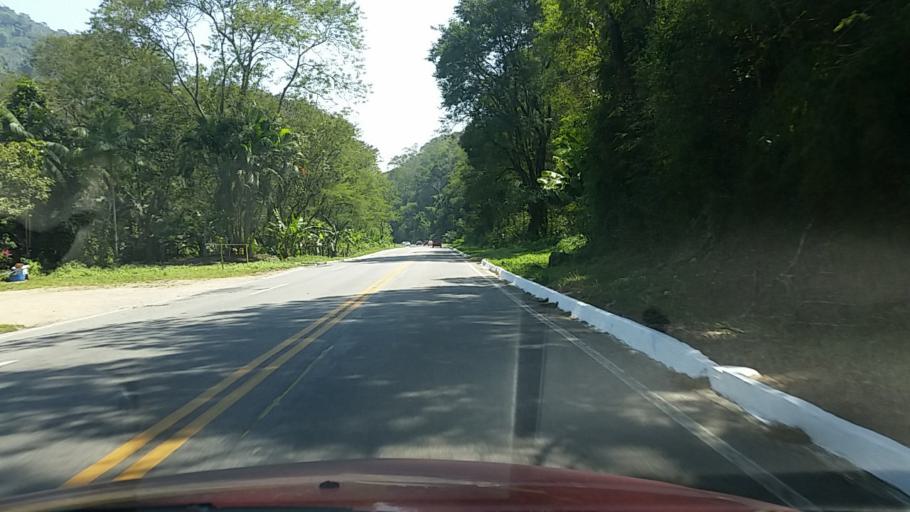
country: BR
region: Sao Paulo
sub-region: Miracatu
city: Miracatu
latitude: -24.3365
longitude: -47.5015
